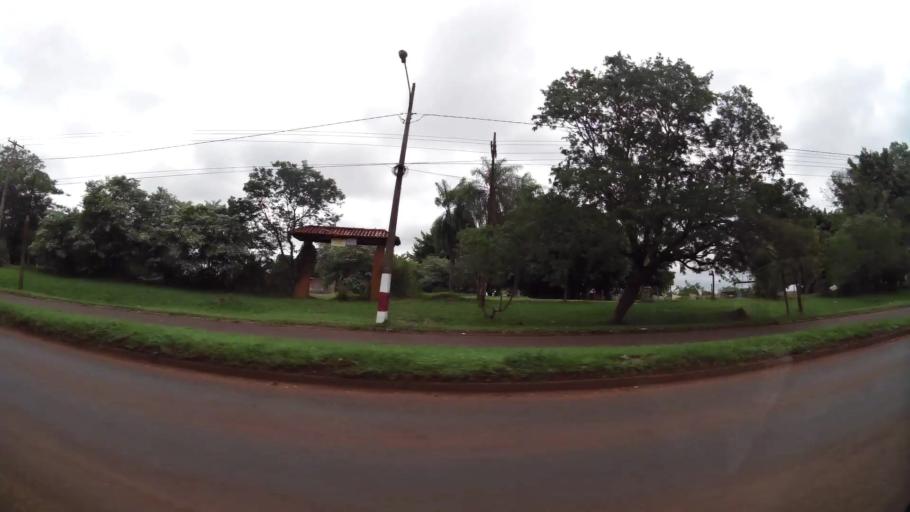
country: PY
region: Alto Parana
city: Ciudad del Este
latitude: -25.4302
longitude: -54.6389
